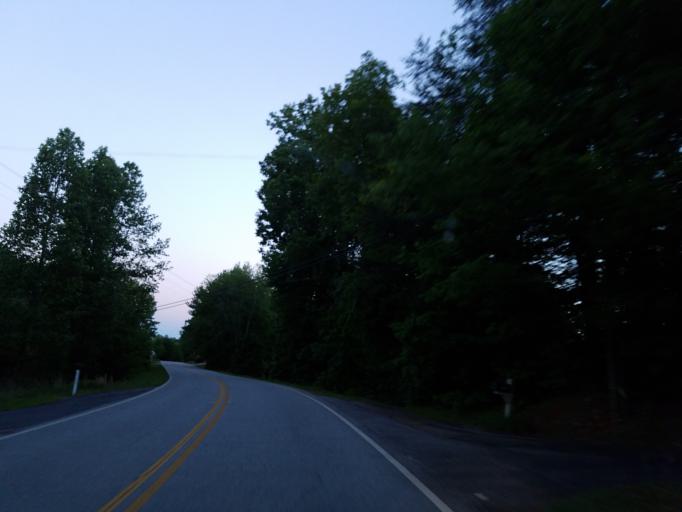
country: US
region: Georgia
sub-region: Lumpkin County
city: Dahlonega
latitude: 34.5962
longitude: -83.9707
